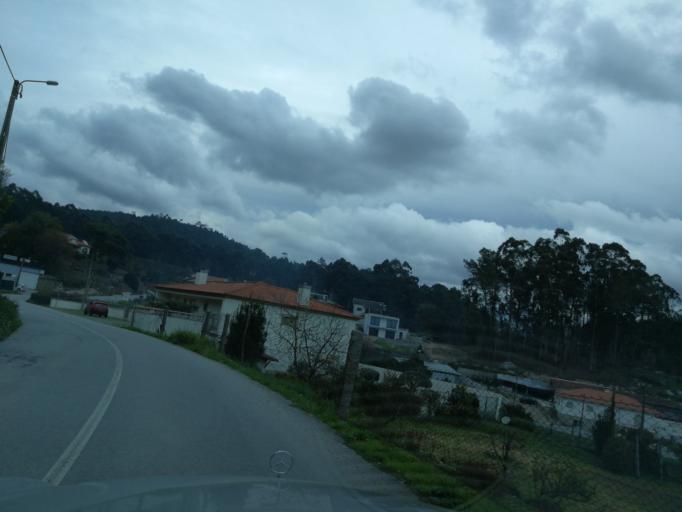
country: PT
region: Braga
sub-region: Braga
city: Oliveira
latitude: 41.4798
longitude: -8.4645
